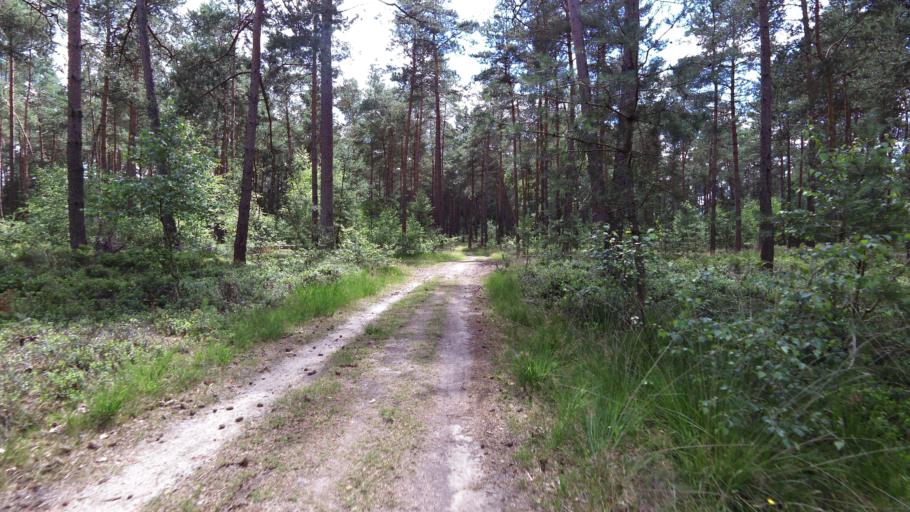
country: NL
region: Gelderland
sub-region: Gemeente Epe
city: Vaassen
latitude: 52.2575
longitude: 5.8983
